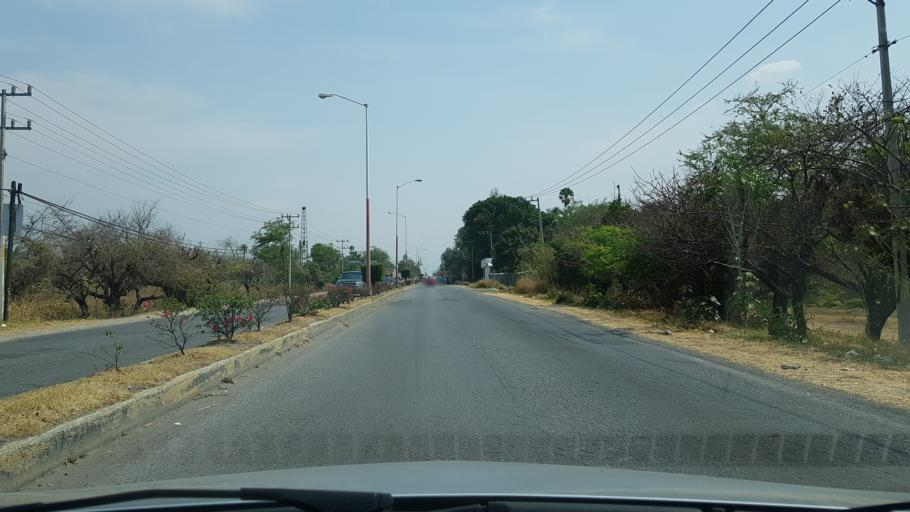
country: MX
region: Morelos
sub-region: Xochitepec
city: Chiconcuac
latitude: 18.7868
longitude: -99.2047
